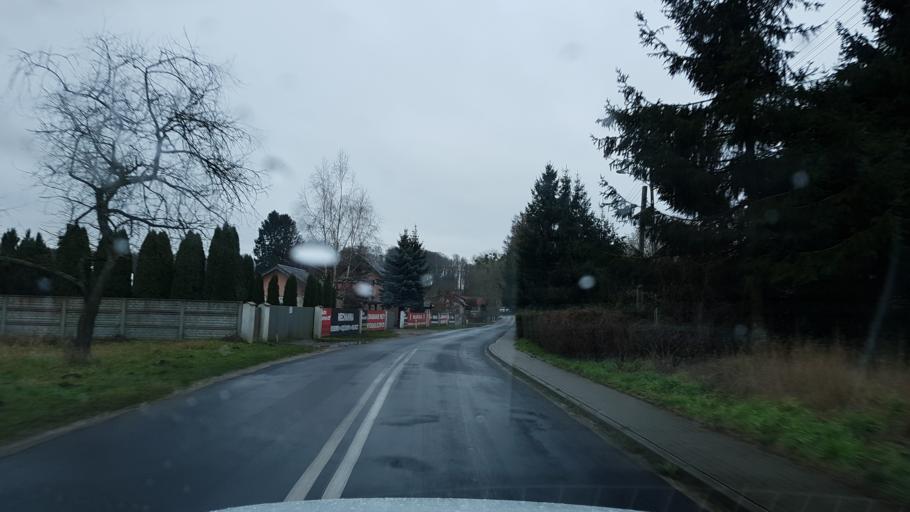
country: PL
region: West Pomeranian Voivodeship
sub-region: Powiat lobeski
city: Radowo Male
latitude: 53.6537
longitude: 15.5286
